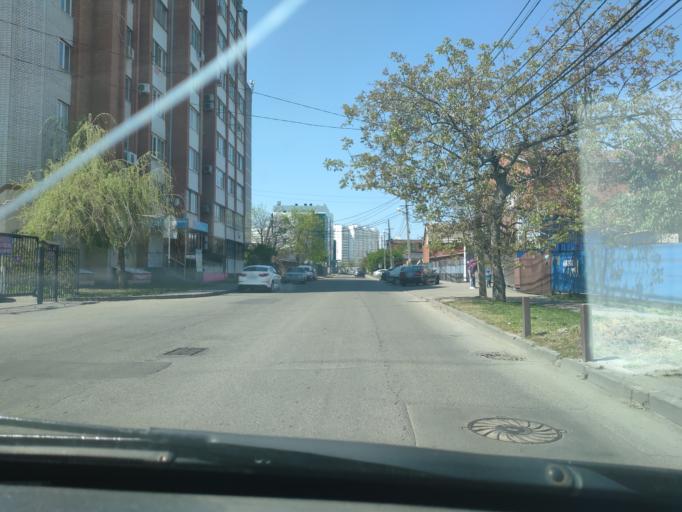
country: RU
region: Krasnodarskiy
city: Krasnodar
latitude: 45.0655
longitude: 39.0213
